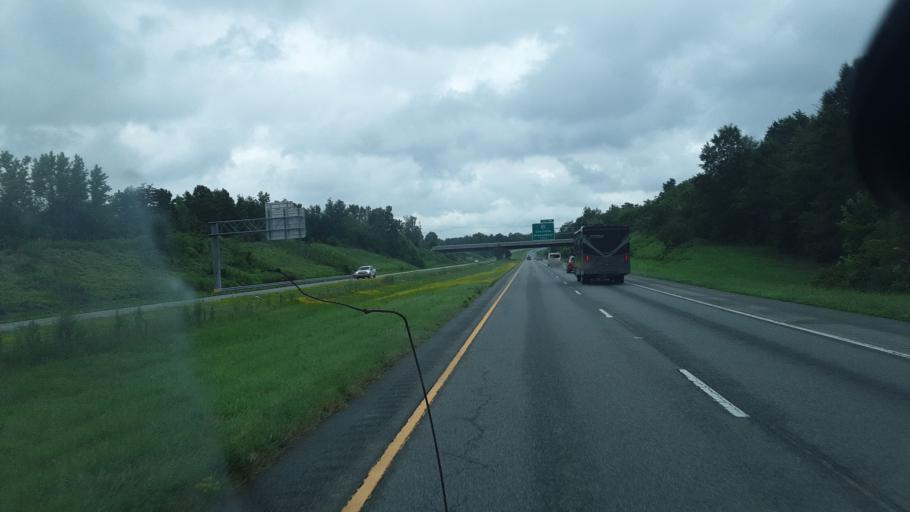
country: US
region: North Carolina
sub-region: Randolph County
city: Archdale
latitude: 35.9360
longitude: -79.9513
